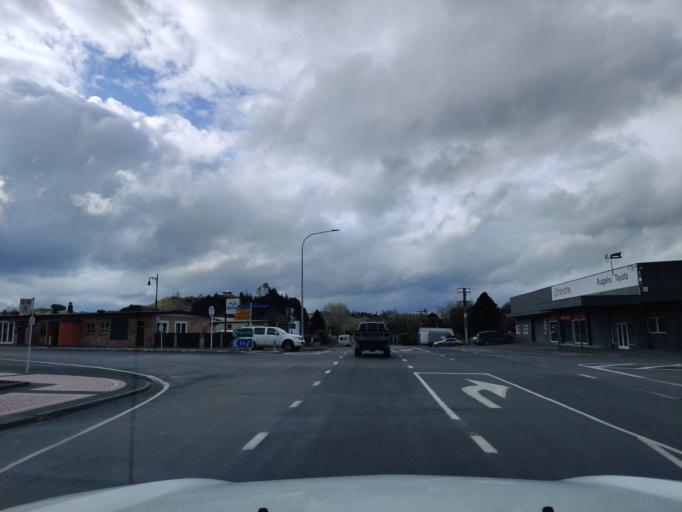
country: NZ
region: Manawatu-Wanganui
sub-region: Ruapehu District
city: Waiouru
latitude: -39.4279
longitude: 175.2818
